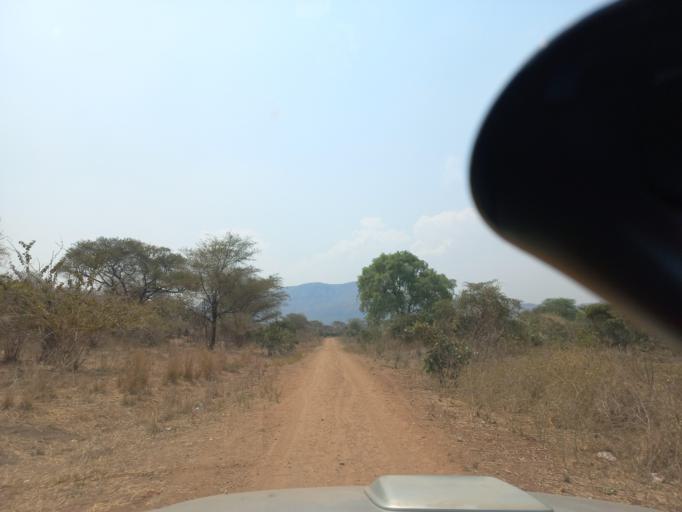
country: ZW
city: Chirundu
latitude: -15.9100
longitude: 28.6868
